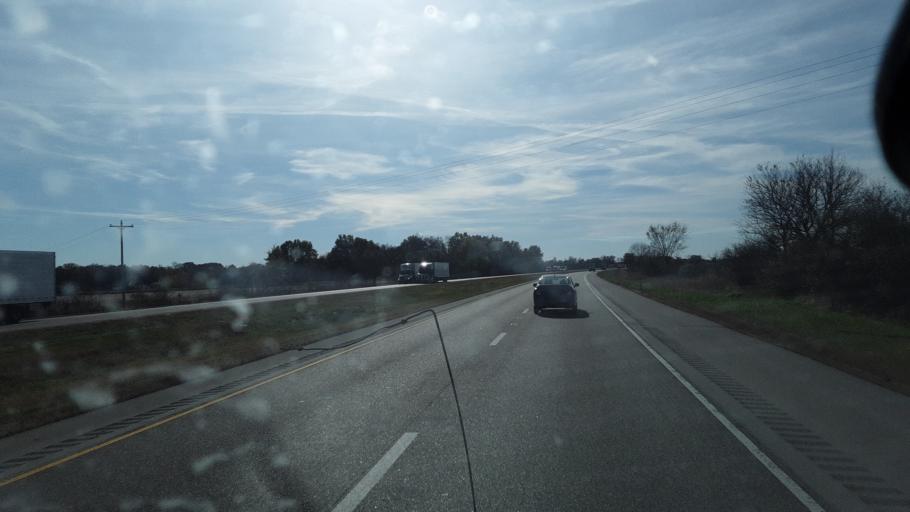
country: US
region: Illinois
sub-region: Cumberland County
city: Greenup
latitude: 39.2402
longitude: -88.1971
